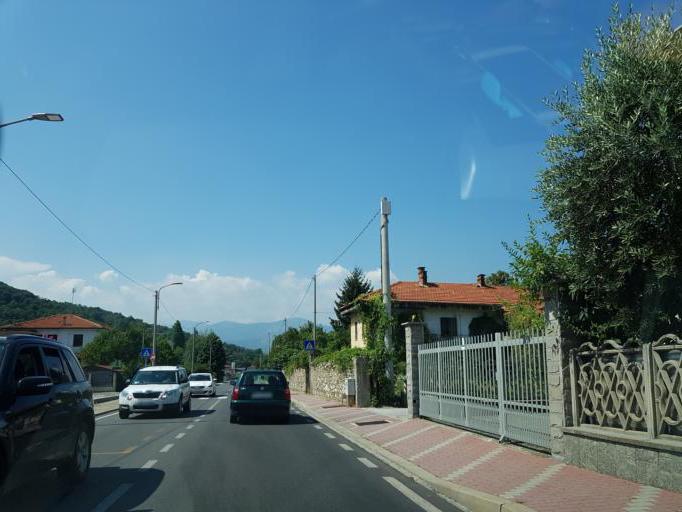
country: IT
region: Piedmont
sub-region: Provincia di Cuneo
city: Caraglio
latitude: 44.4231
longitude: 7.4302
